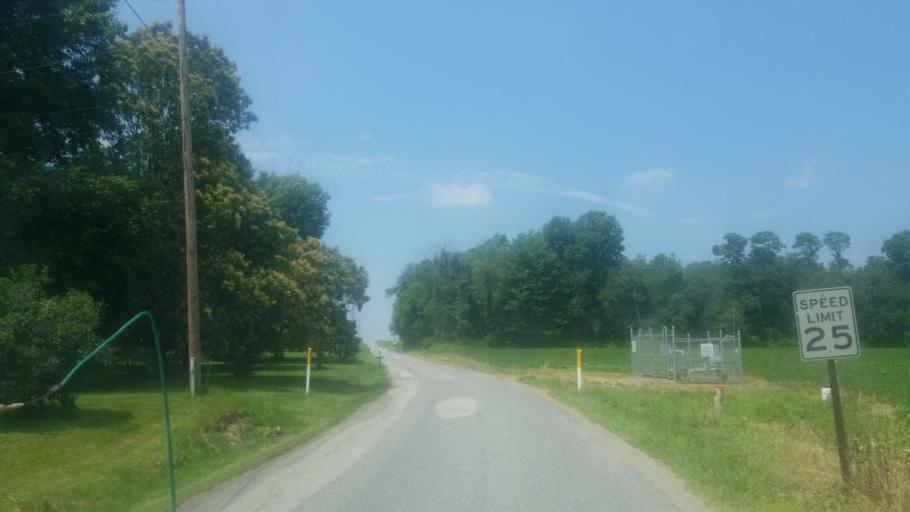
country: US
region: Ohio
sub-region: Columbiana County
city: Columbiana
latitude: 40.9224
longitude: -80.7074
